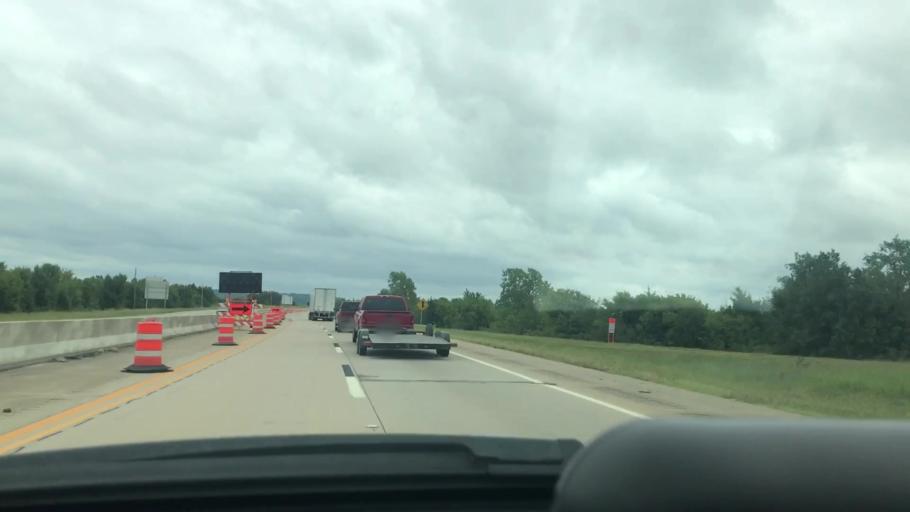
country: US
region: Oklahoma
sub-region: McIntosh County
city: Eufaula
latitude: 35.2171
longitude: -95.6104
